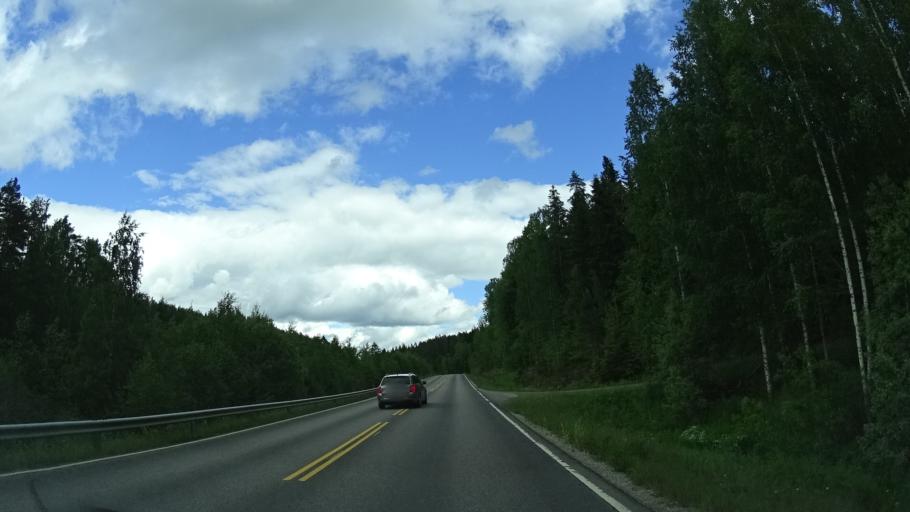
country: FI
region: Paijanne Tavastia
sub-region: Lahti
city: Asikkala
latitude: 61.3379
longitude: 25.5845
